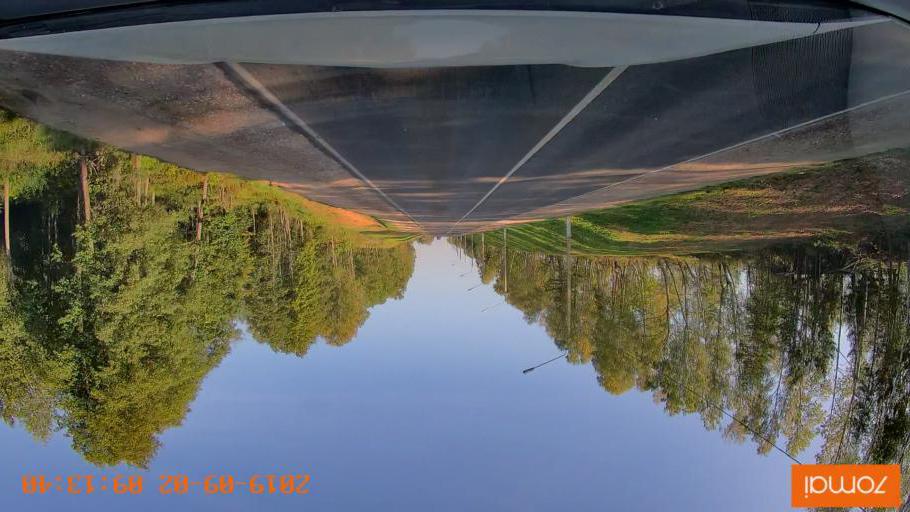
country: RU
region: Kaluga
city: Nikola-Lenivets
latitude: 54.8513
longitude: 35.5291
